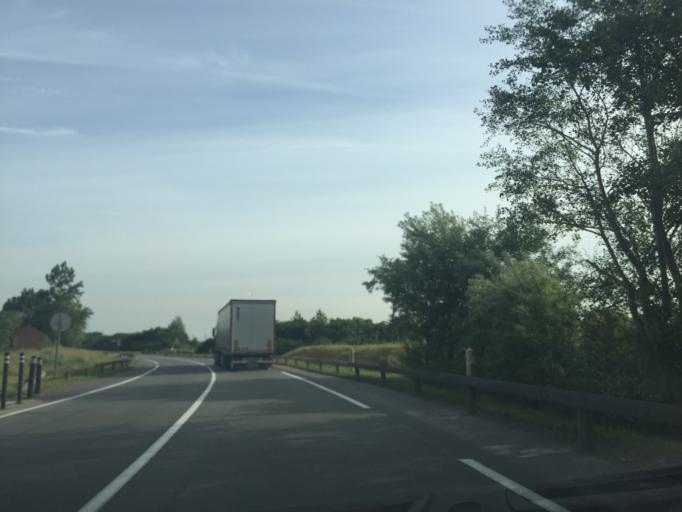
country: FR
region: Nord-Pas-de-Calais
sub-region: Departement du Nord
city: Loon-Plage
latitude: 51.0030
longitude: 2.1976
